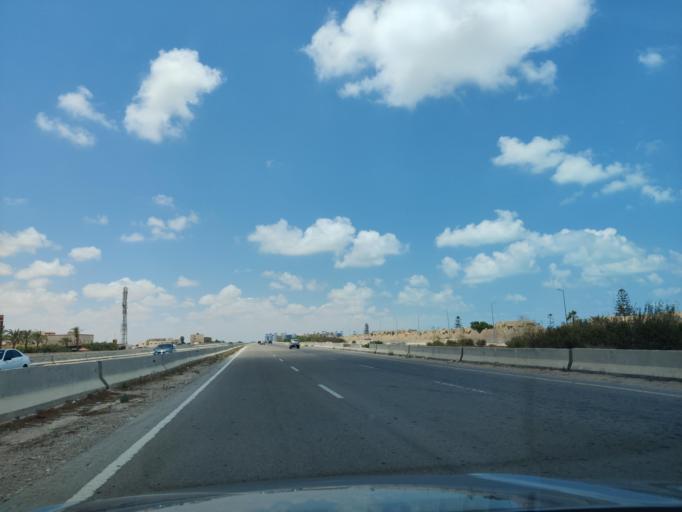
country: EG
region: Muhafazat Matruh
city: Al `Alamayn
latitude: 30.8189
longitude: 29.0239
